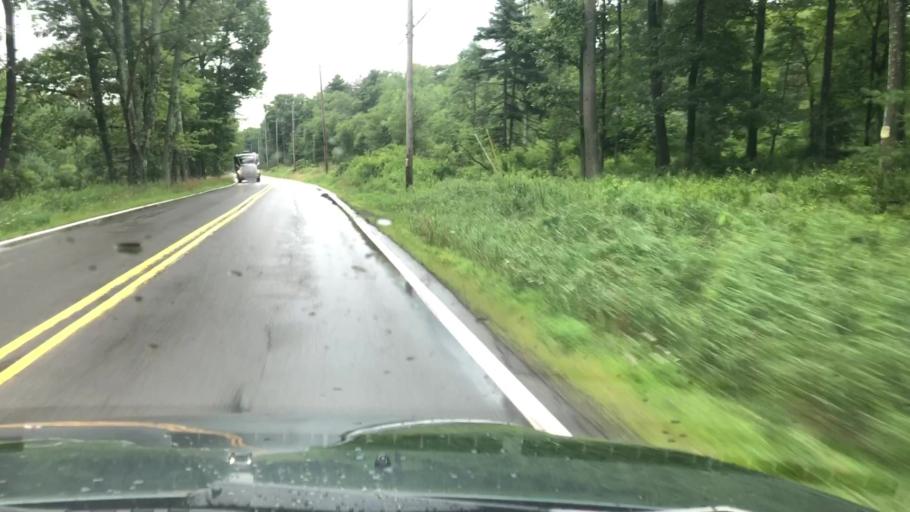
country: US
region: Pennsylvania
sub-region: Wayne County
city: Hawley
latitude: 41.3325
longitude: -75.2042
